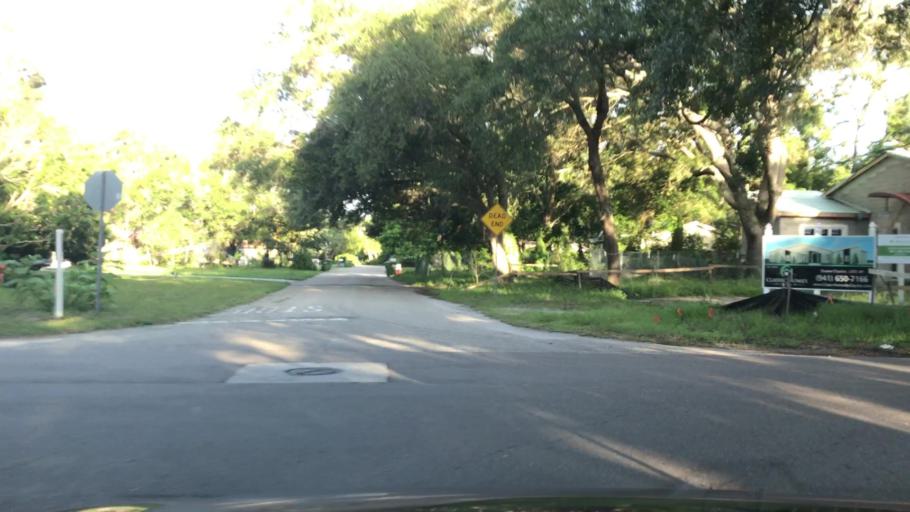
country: US
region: Florida
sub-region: Sarasota County
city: Sarasota
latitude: 27.3356
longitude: -82.5159
